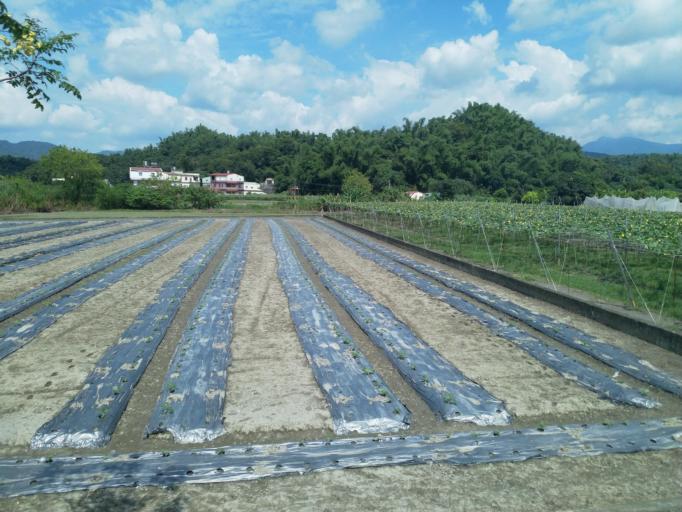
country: TW
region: Taiwan
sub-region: Pingtung
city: Pingtung
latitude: 22.8808
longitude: 120.5611
